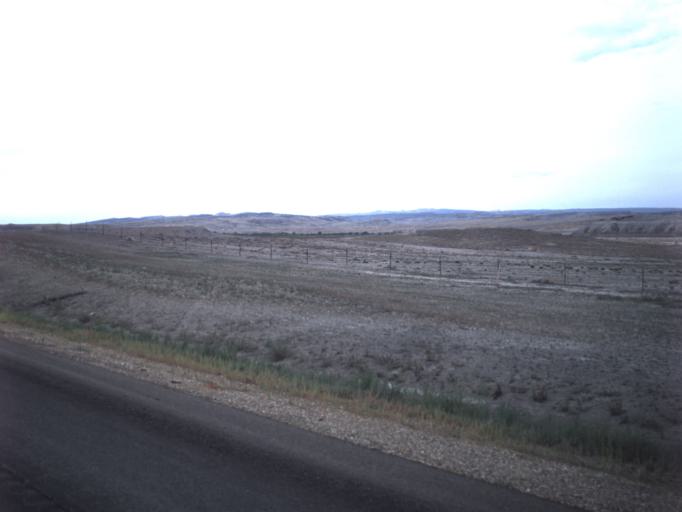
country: US
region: Utah
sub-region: Carbon County
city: East Carbon City
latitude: 39.3210
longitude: -110.3650
